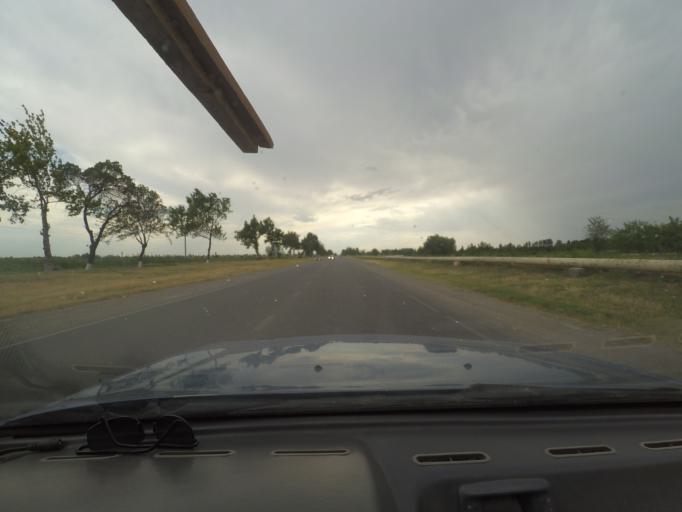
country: UZ
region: Sirdaryo
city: Guliston
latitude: 40.4921
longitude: 68.8352
